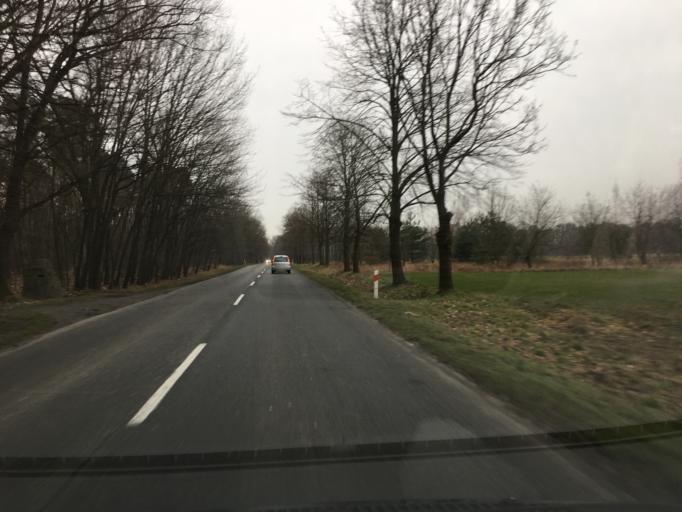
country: PL
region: Opole Voivodeship
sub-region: Powiat kedzierzynsko-kozielski
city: Bierawa
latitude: 50.3024
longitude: 18.2308
